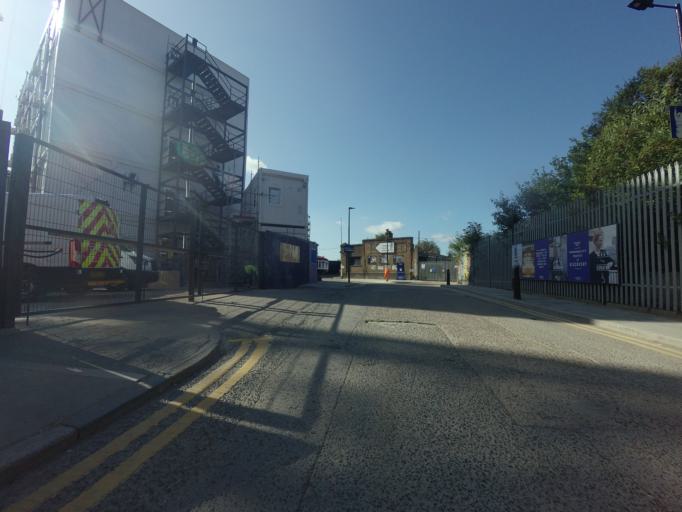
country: GB
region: England
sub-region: Greater London
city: Poplar
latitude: 51.5091
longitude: 0.0053
